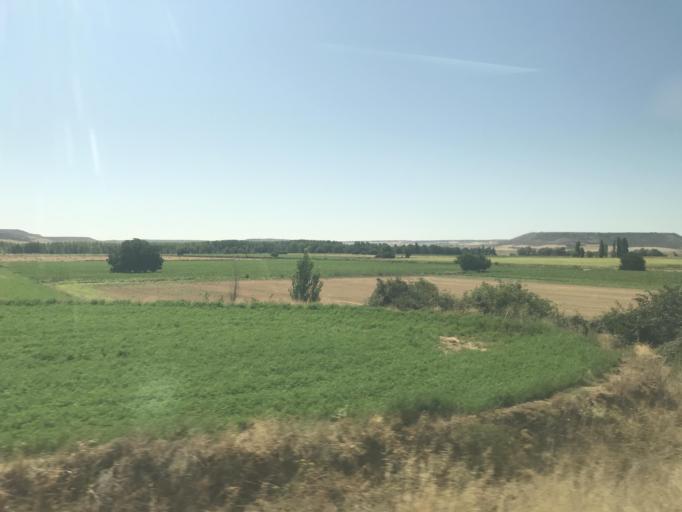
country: ES
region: Castille and Leon
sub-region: Provincia de Palencia
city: Torquemada
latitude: 42.0067
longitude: -4.3472
